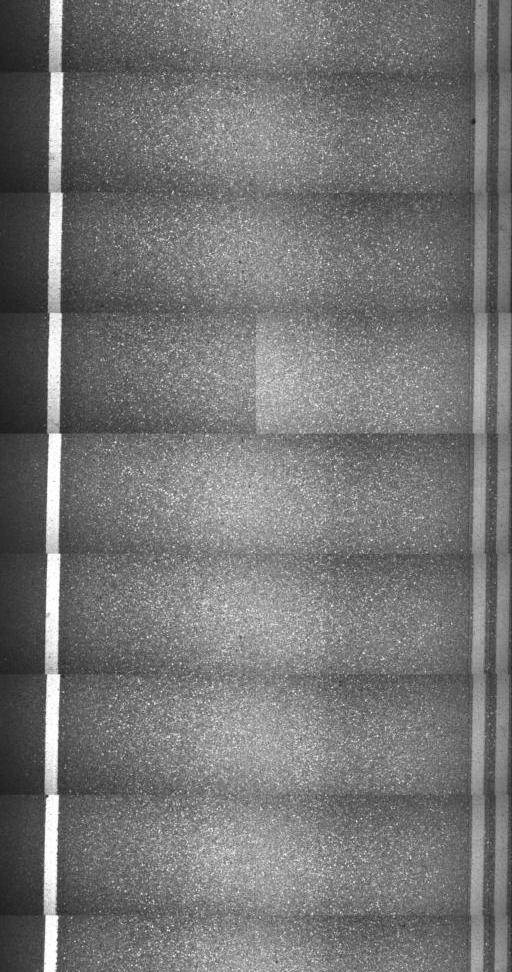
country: US
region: Vermont
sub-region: Lamoille County
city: Morrisville
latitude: 44.5693
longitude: -72.6028
